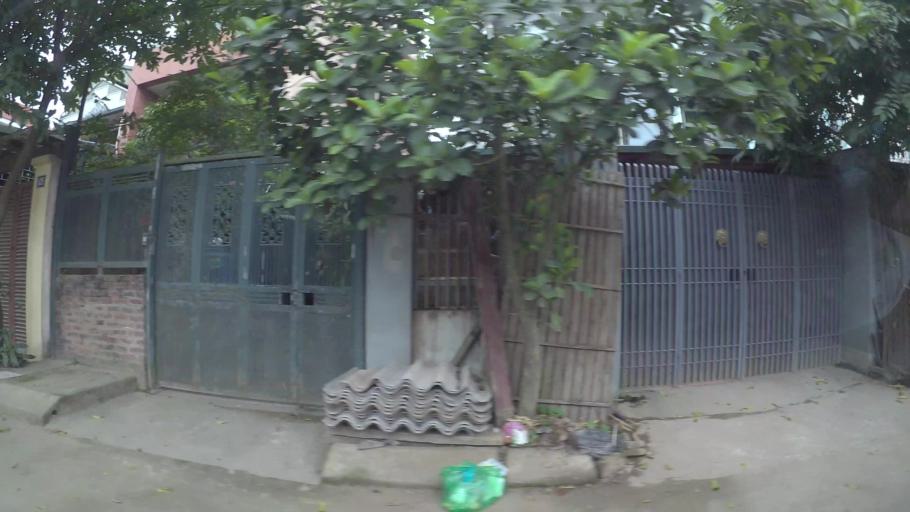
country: VN
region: Ha Noi
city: Tay Ho
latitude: 21.0767
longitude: 105.8249
